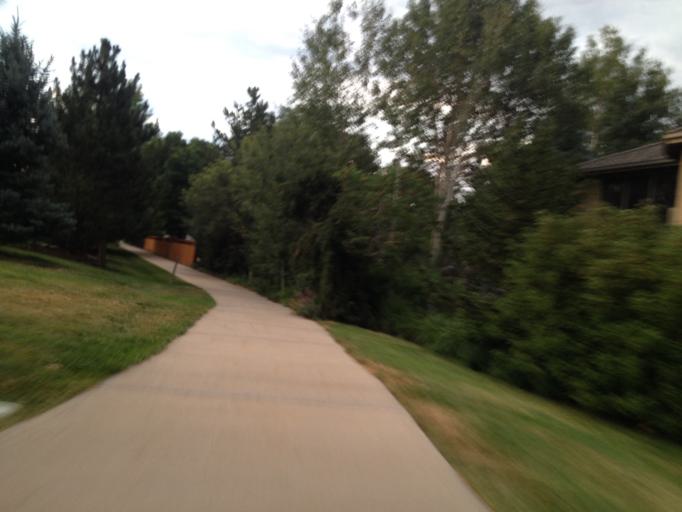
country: US
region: Colorado
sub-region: Boulder County
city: Superior
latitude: 39.9625
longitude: -105.1539
